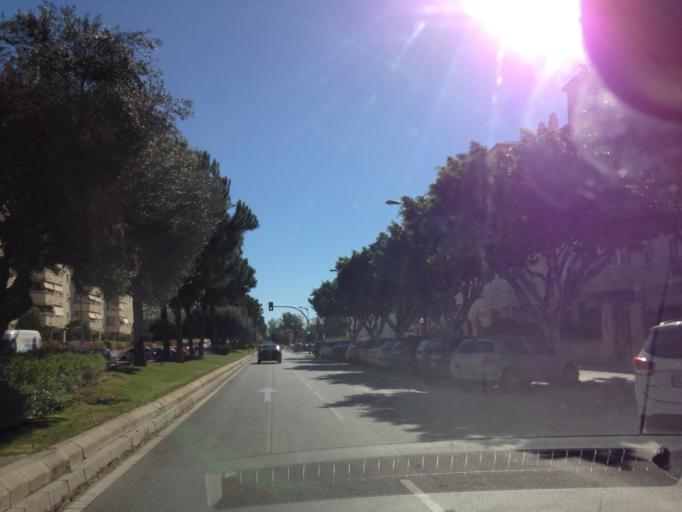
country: ES
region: Andalusia
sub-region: Provincia de Malaga
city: Malaga
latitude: 36.6885
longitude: -4.4545
